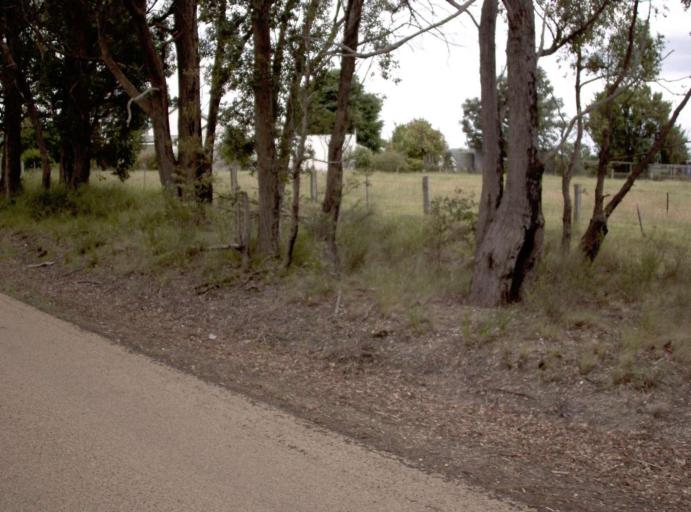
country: AU
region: Victoria
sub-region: East Gippsland
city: Bairnsdale
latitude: -37.7399
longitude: 147.5972
